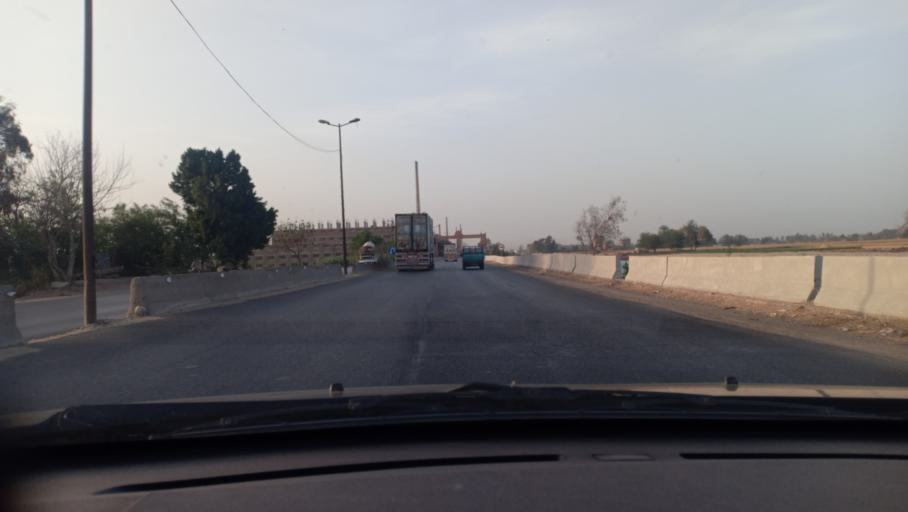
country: EG
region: Muhafazat al Gharbiyah
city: Zifta
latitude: 30.6008
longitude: 31.2745
